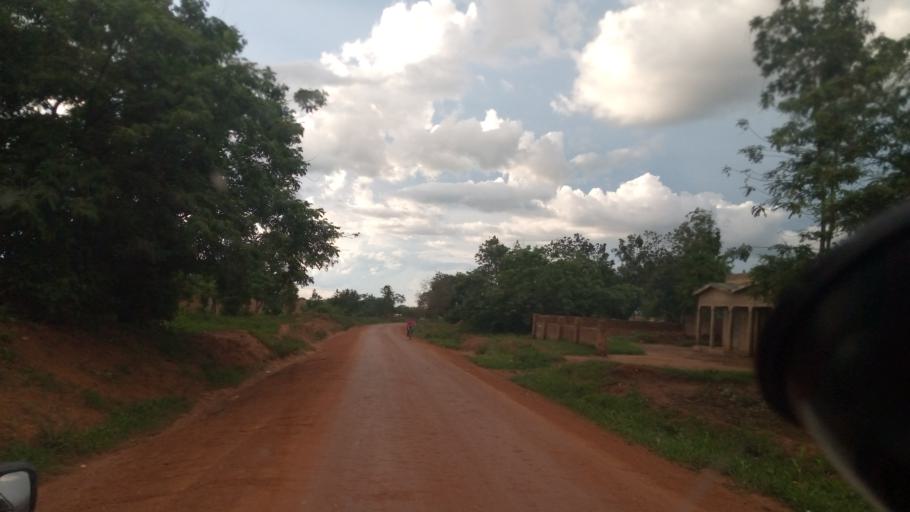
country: UG
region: Northern Region
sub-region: Lira District
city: Lira
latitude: 2.3758
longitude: 32.9338
